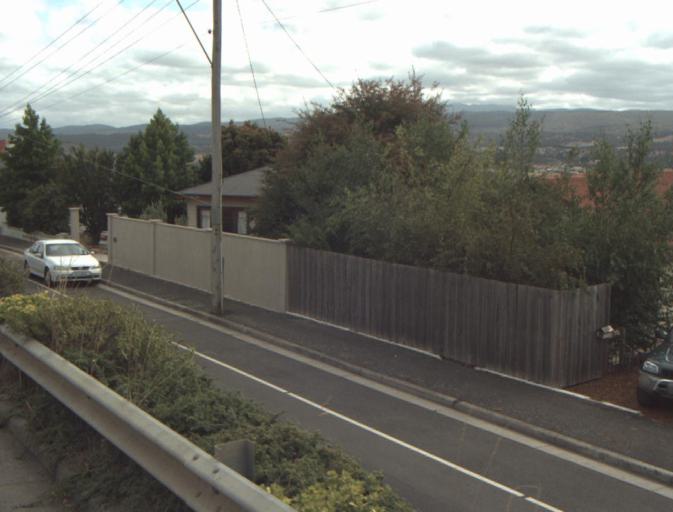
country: AU
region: Tasmania
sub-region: Launceston
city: East Launceston
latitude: -41.4508
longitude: 147.1537
